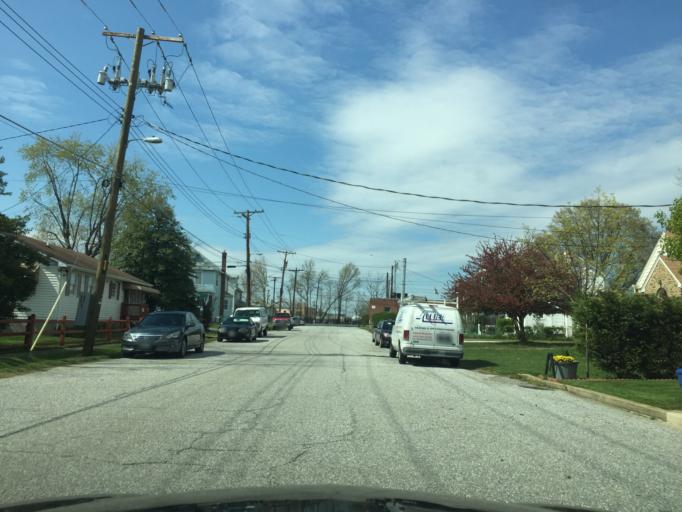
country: US
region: Maryland
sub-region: Baltimore County
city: Middle River
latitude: 39.3306
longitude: -76.4406
